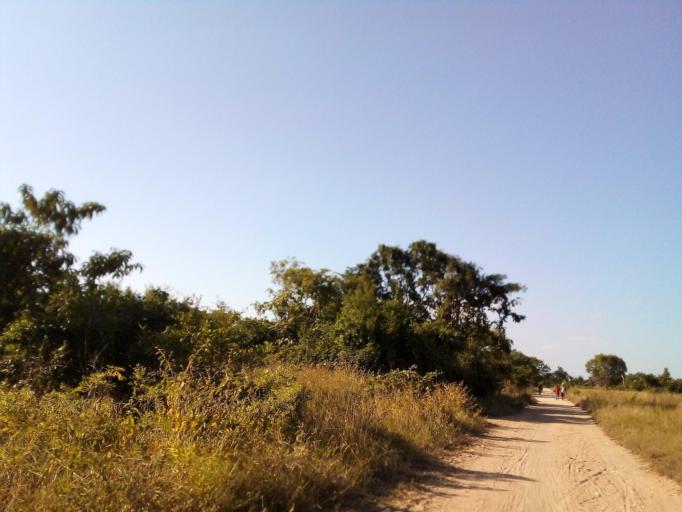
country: MZ
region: Zambezia
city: Quelimane
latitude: -17.5241
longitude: 36.6819
